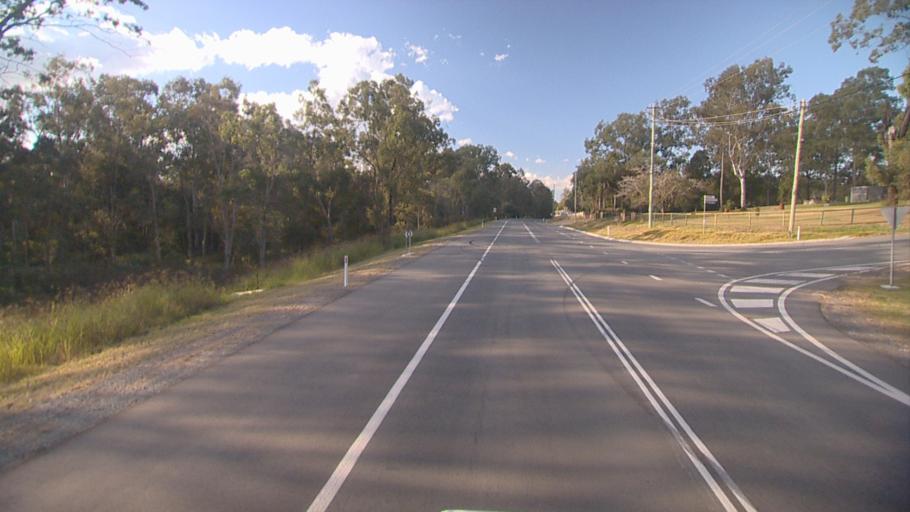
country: AU
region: Queensland
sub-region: Ipswich
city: Springfield Lakes
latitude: -27.7244
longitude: 152.9579
